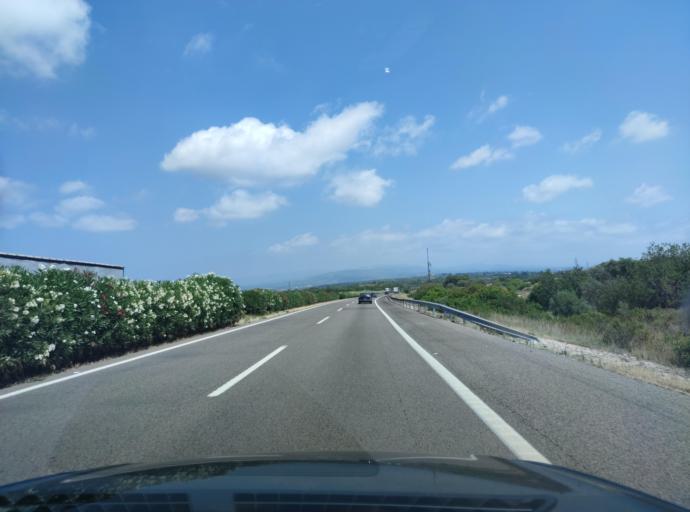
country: ES
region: Catalonia
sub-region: Provincia de Tarragona
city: Masdenverge
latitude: 40.6846
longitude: 0.5259
